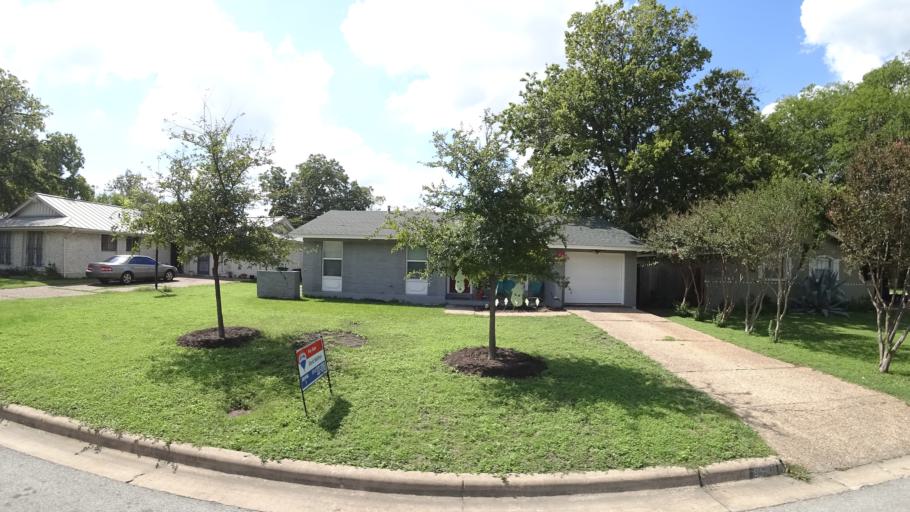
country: US
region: Texas
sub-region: Travis County
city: Wells Branch
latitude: 30.3634
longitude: -97.7211
